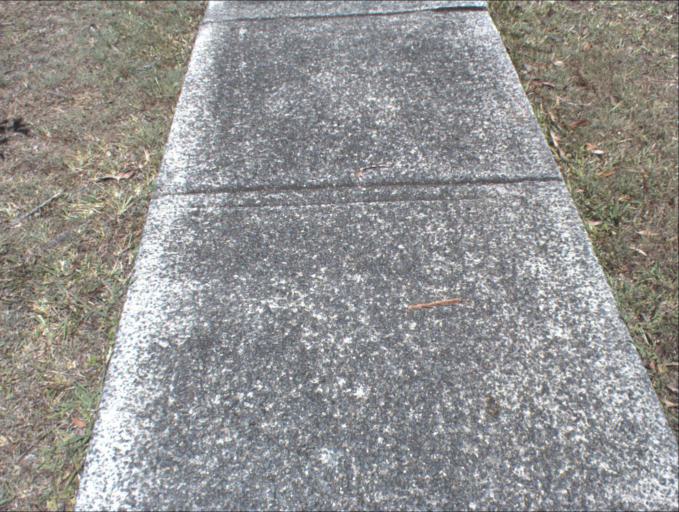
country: AU
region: Queensland
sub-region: Gold Coast
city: Yatala
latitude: -27.7028
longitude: 153.2242
